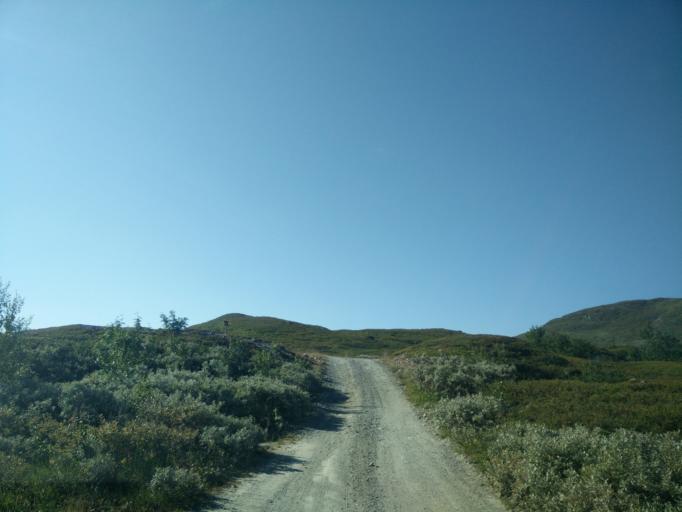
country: NO
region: Sor-Trondelag
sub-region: Tydal
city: Aas
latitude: 62.5738
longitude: 12.2002
